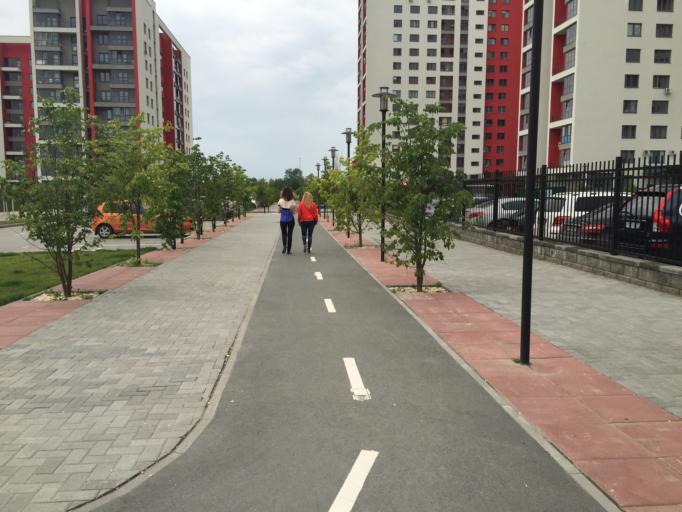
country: RU
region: Tjumen
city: Tyumen
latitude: 57.1709
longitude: 65.5578
